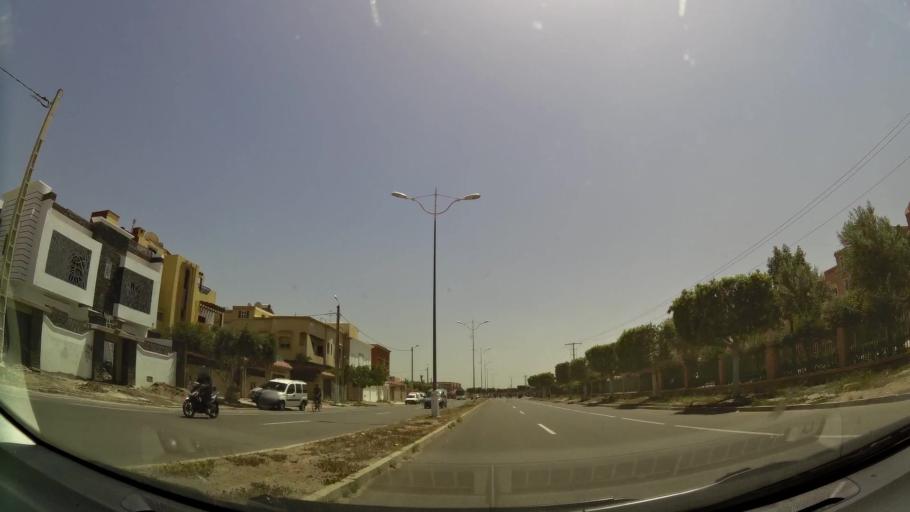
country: MA
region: Souss-Massa-Draa
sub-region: Inezgane-Ait Mellou
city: Inezgane
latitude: 30.3443
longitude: -9.4834
